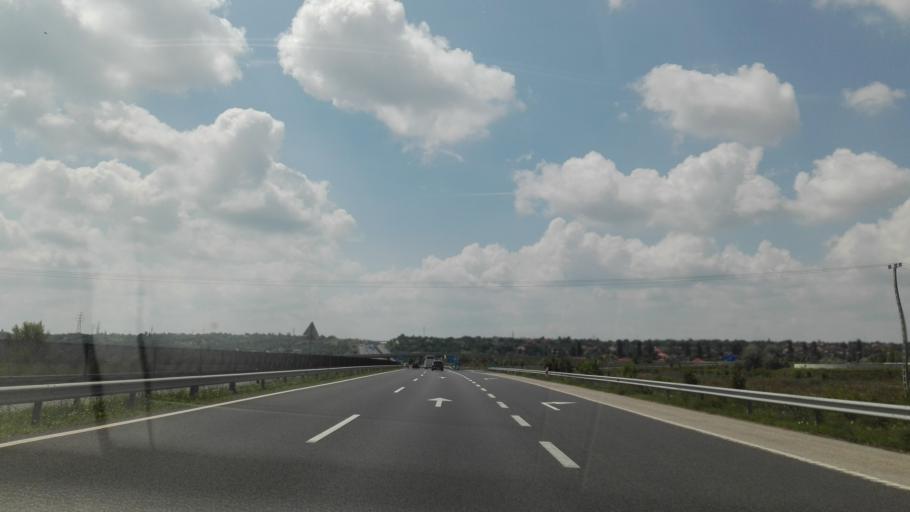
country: HU
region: Pest
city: Erd
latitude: 47.3722
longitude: 18.9391
